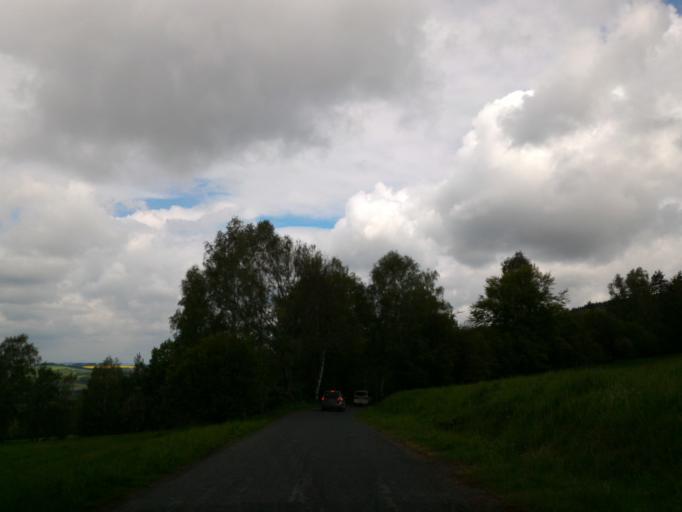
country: CZ
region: Vysocina
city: Ledec nad Sazavou
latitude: 49.6147
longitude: 15.2739
